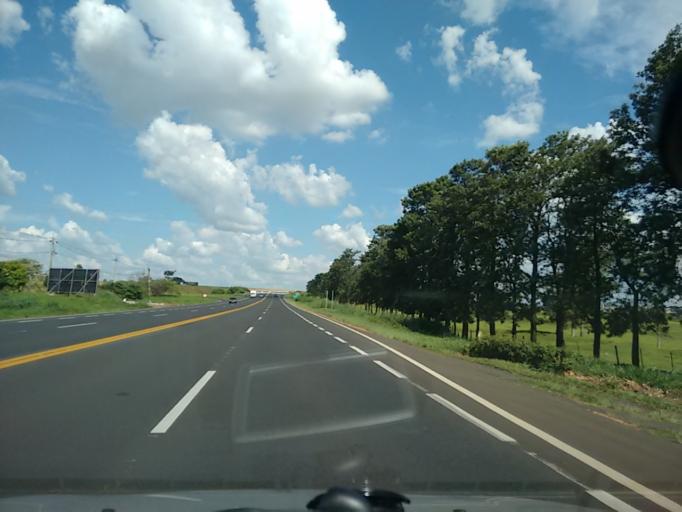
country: BR
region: Sao Paulo
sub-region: Marilia
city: Marilia
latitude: -22.1764
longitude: -49.9765
